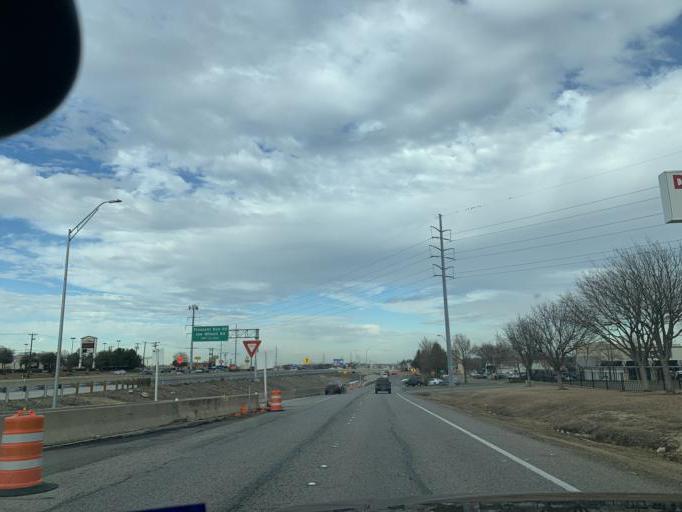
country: US
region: Texas
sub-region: Dallas County
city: Cedar Hill
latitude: 32.5921
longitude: -96.9433
